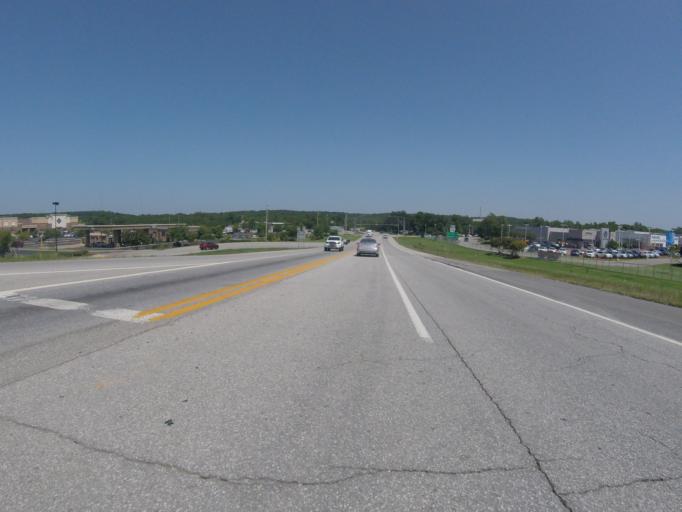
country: US
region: Arkansas
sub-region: Washington County
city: Johnson
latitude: 36.1069
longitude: -94.1799
